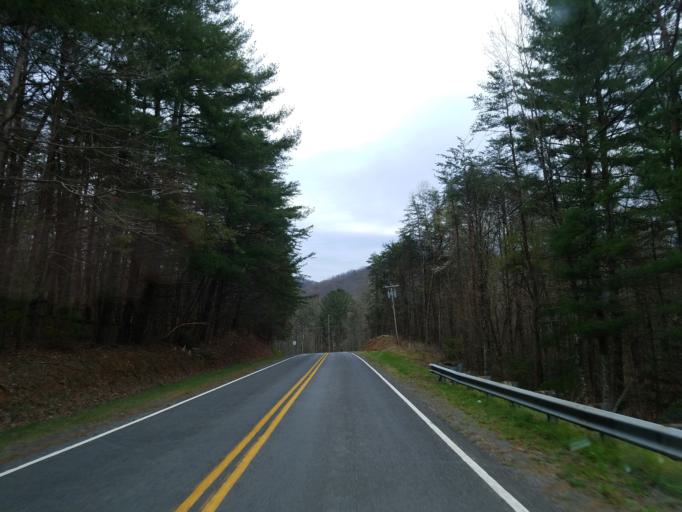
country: US
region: Georgia
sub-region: Fannin County
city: Blue Ridge
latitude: 34.6715
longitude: -84.2820
